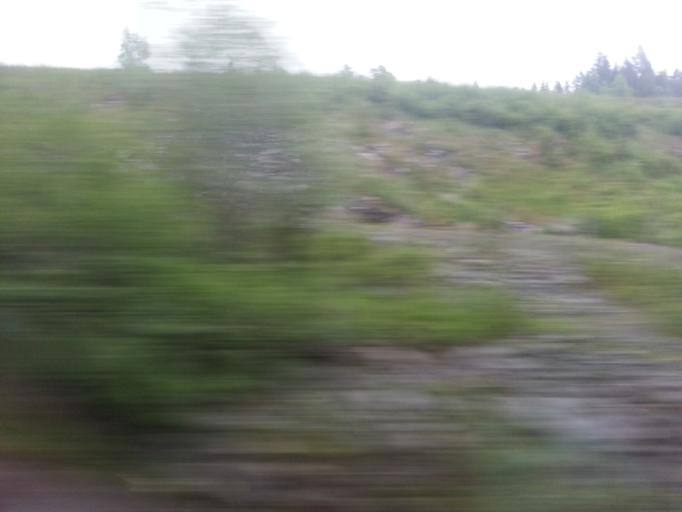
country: NO
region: Sor-Trondelag
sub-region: Rennebu
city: Berkak
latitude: 62.7424
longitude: 9.9835
